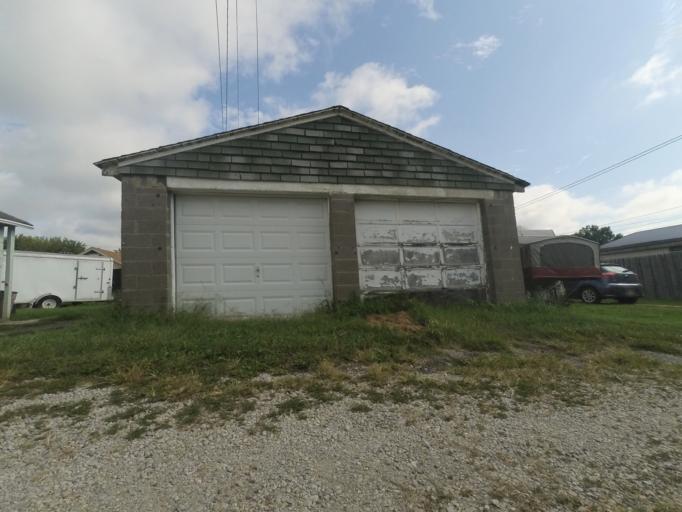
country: US
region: West Virginia
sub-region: Cabell County
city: Huntington
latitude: 38.4346
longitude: -82.4029
